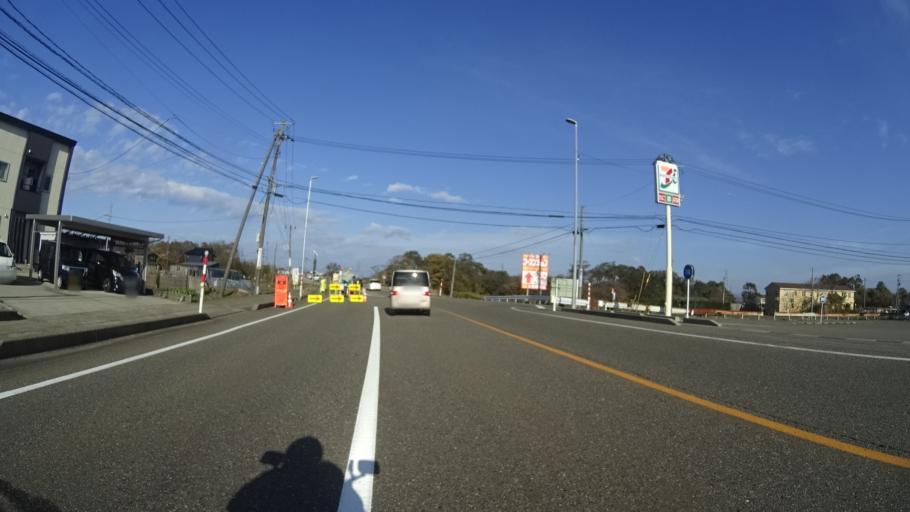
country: JP
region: Niigata
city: Joetsu
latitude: 37.2042
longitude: 138.2989
